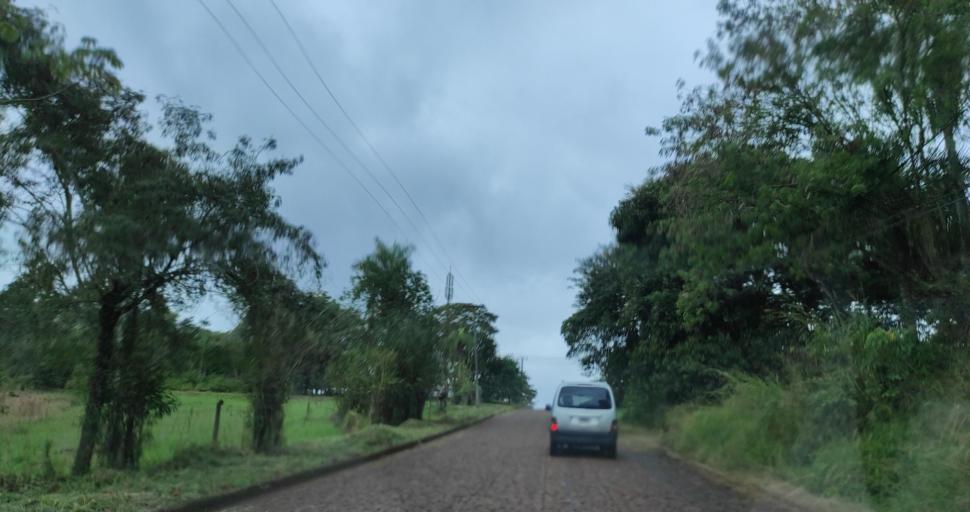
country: AR
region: Misiones
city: Puerto Rico
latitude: -26.7958
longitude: -55.0191
